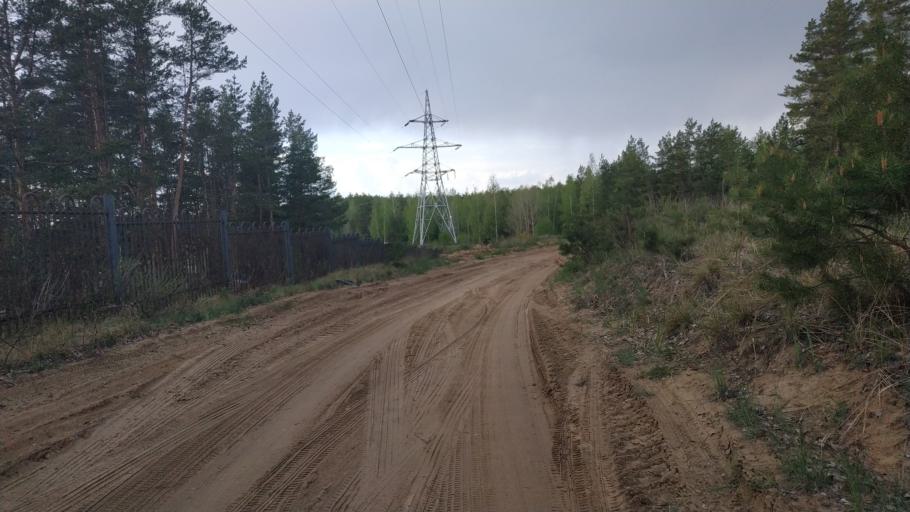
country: RU
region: Chuvashia
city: Novocheboksarsk
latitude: 56.1605
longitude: 47.4644
